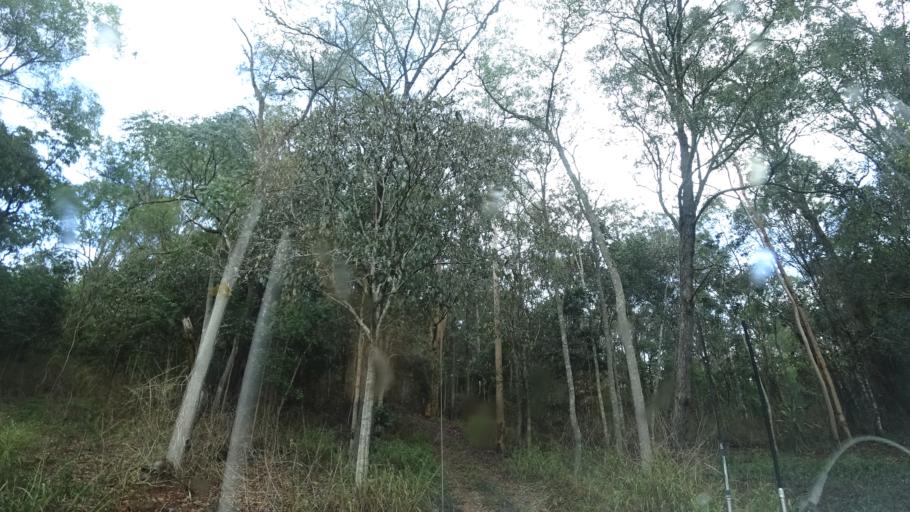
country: AU
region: Queensland
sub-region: Brisbane
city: Pullenvale
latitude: -27.4536
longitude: 152.8729
